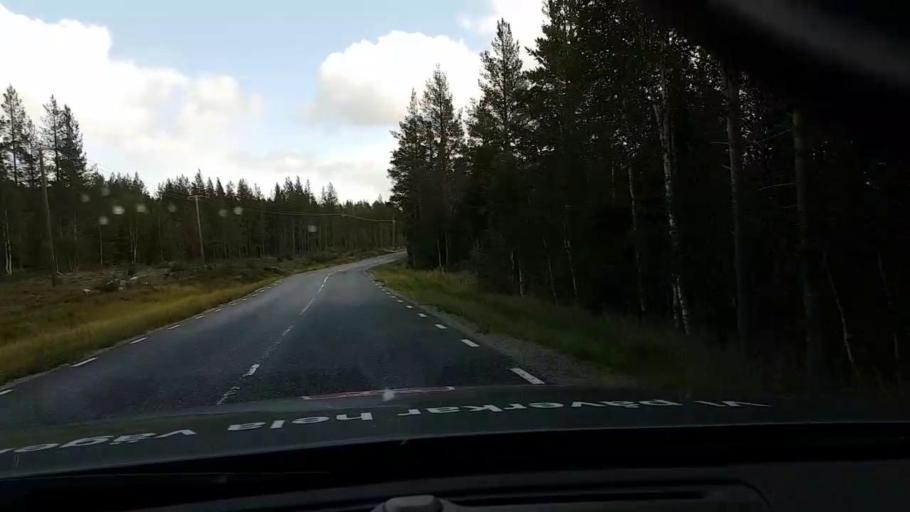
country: SE
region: Vaesterbotten
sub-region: Asele Kommun
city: Asele
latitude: 63.8108
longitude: 17.5256
